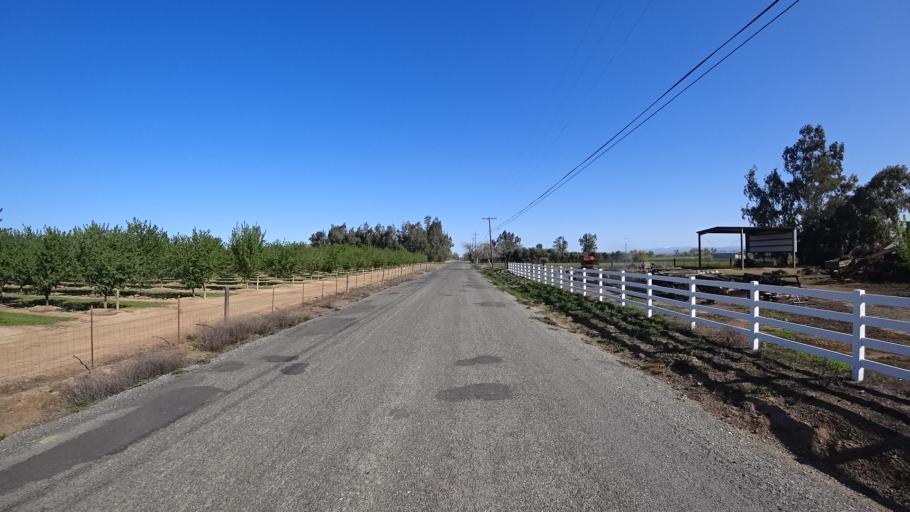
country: US
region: California
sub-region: Glenn County
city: Hamilton City
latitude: 39.7806
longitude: -122.0666
